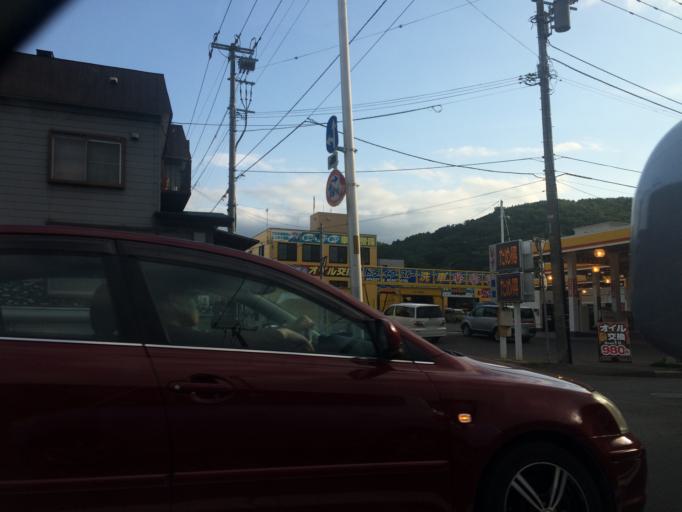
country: JP
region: Hokkaido
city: Sapporo
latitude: 43.0100
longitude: 141.3459
